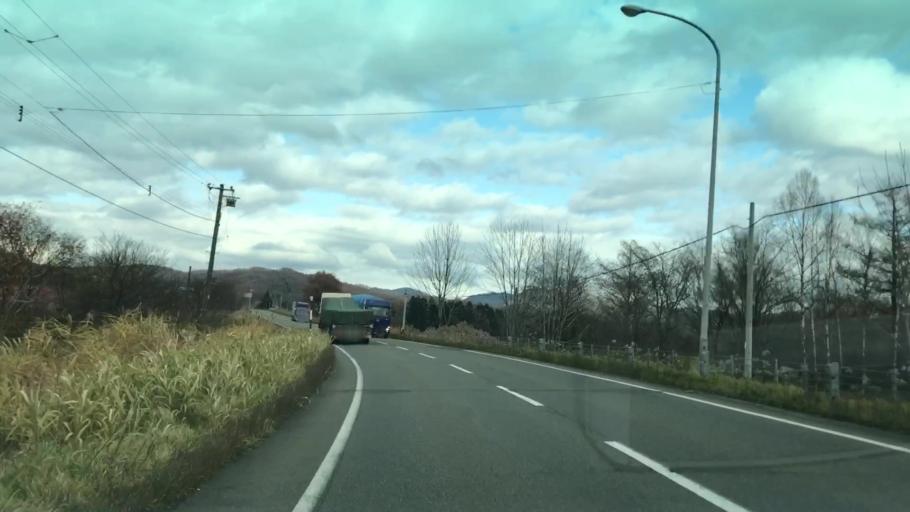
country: JP
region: Hokkaido
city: Shimo-furano
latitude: 42.8676
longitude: 142.4259
